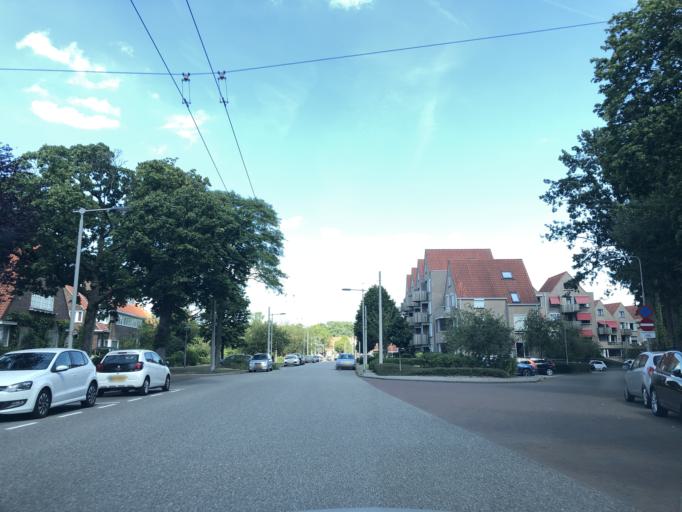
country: NL
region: Gelderland
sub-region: Gemeente Arnhem
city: Burgemeesterswijk
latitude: 52.0021
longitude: 5.9074
